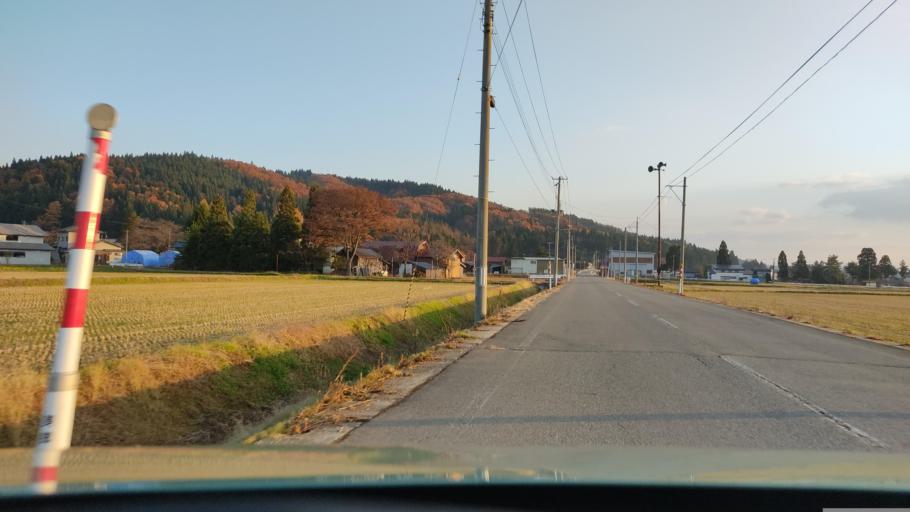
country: JP
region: Akita
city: Omagari
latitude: 39.4503
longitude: 140.5849
